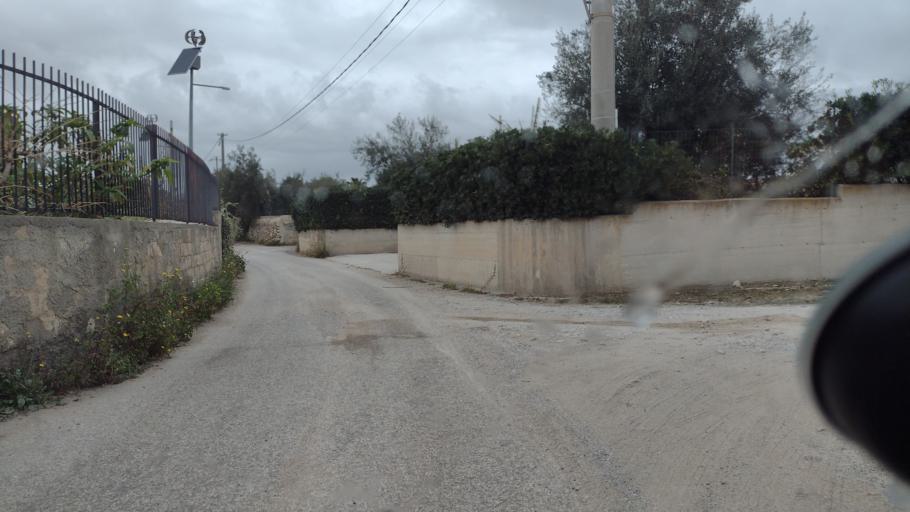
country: IT
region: Sicily
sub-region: Provincia di Siracusa
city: Avola
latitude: 36.8855
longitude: 15.1241
